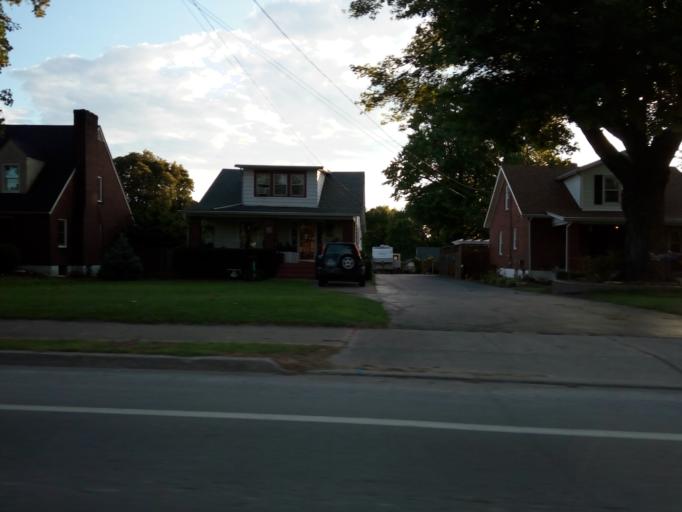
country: US
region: Kentucky
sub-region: Jefferson County
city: Audubon Park
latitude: 38.2034
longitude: -85.7114
